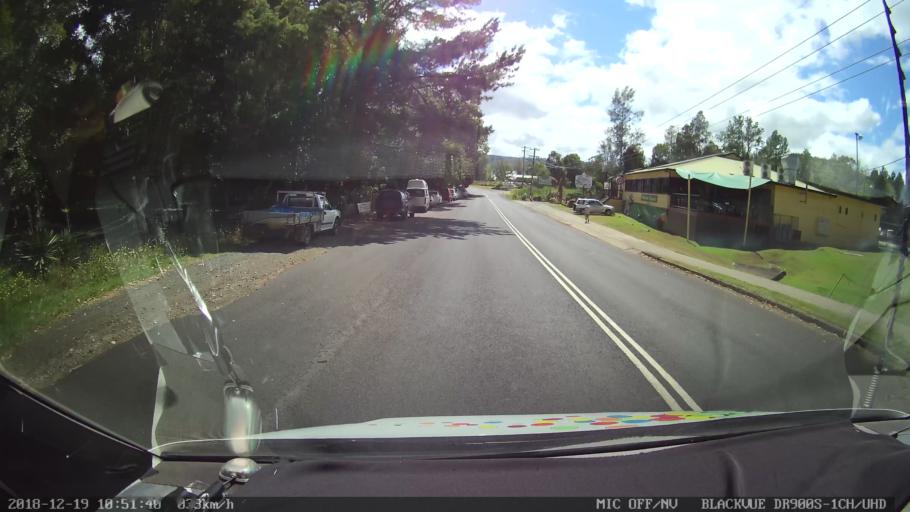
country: AU
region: New South Wales
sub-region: Lismore Municipality
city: Nimbin
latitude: -28.5942
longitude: 153.2246
